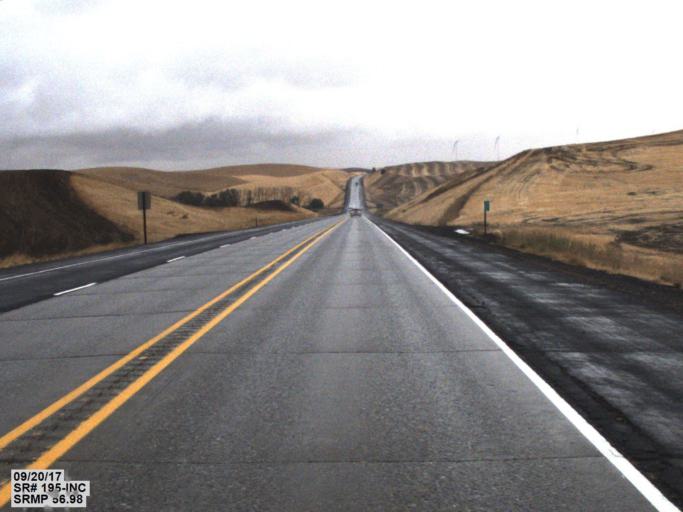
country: US
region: Washington
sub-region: Whitman County
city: Colfax
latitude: 47.1311
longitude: -117.3793
